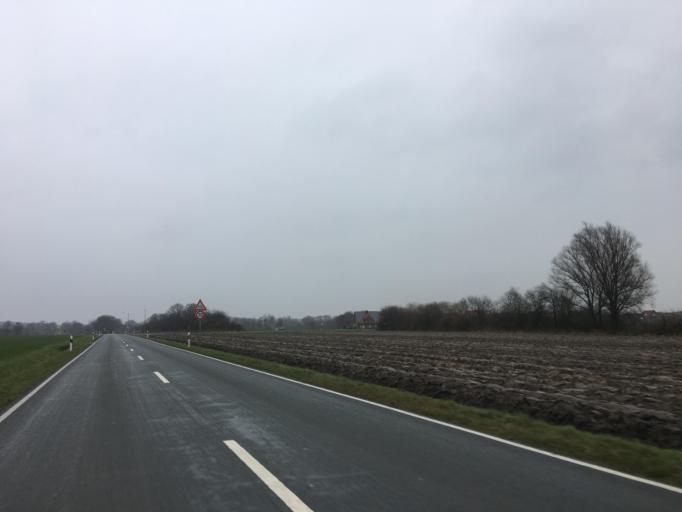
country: DE
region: North Rhine-Westphalia
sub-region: Regierungsbezirk Munster
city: Nottuln
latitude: 51.8595
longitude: 7.3501
